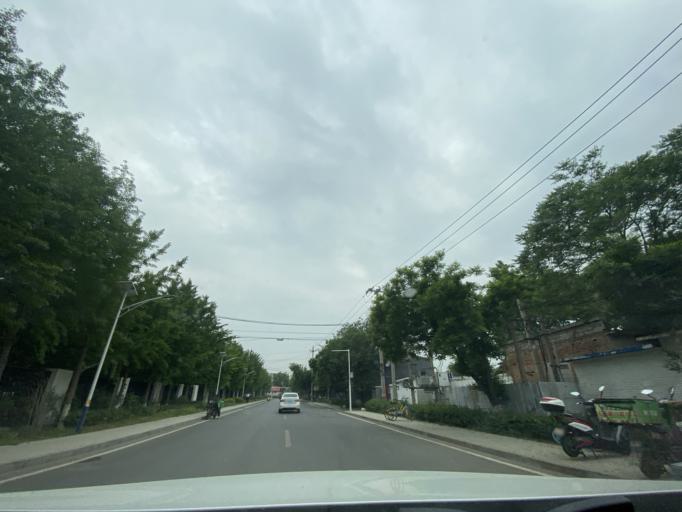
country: CN
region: Beijing
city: Sijiqing
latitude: 39.9352
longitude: 116.2390
